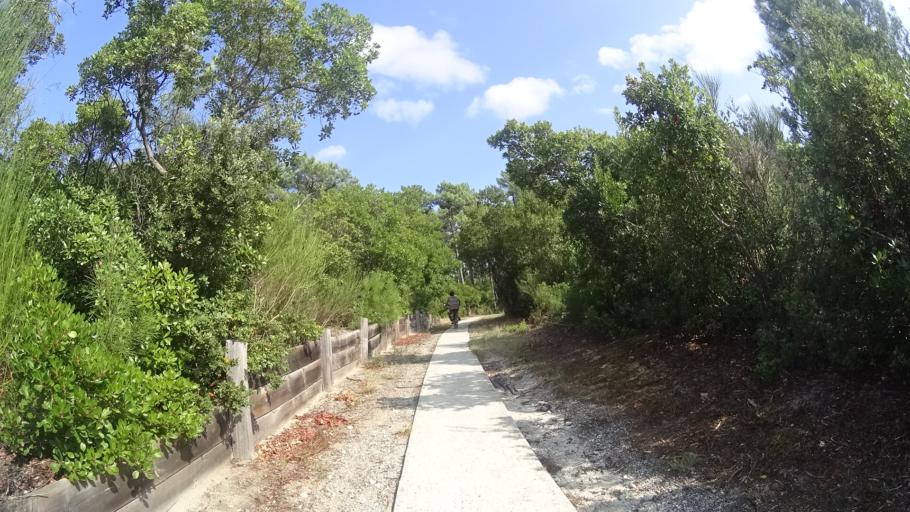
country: FR
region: Aquitaine
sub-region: Departement de la Gironde
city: Lacanau
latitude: 44.9649
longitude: -1.1745
